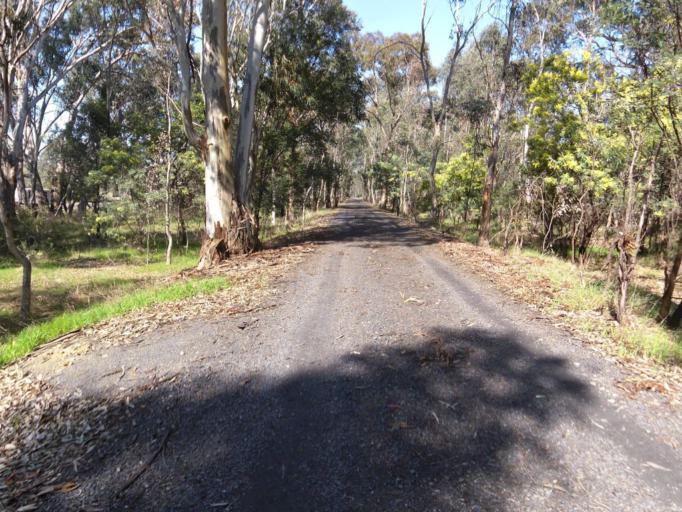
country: AU
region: Victoria
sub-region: Murrindindi
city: Alexandra
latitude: -36.9844
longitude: 145.7283
